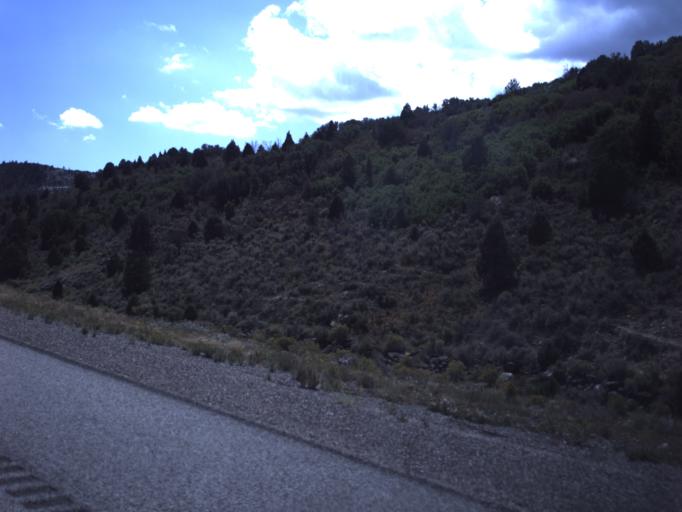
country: US
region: Utah
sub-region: Sevier County
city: Salina
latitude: 38.7855
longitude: -111.4981
